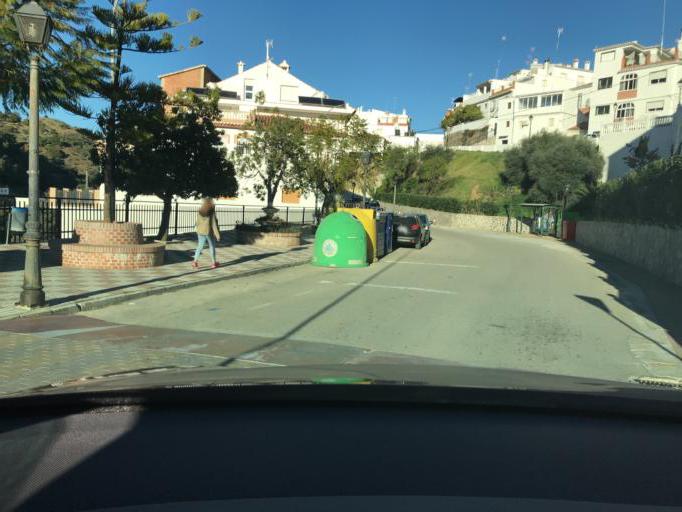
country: ES
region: Andalusia
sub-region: Provincia de Malaga
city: Tolox
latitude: 36.6866
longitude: -4.9029
